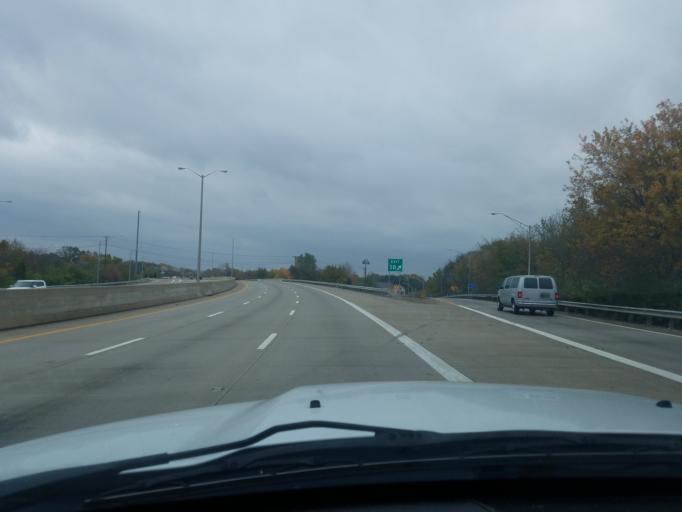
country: US
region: Kentucky
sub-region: Jefferson County
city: Shively
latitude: 38.2082
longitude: -85.8282
